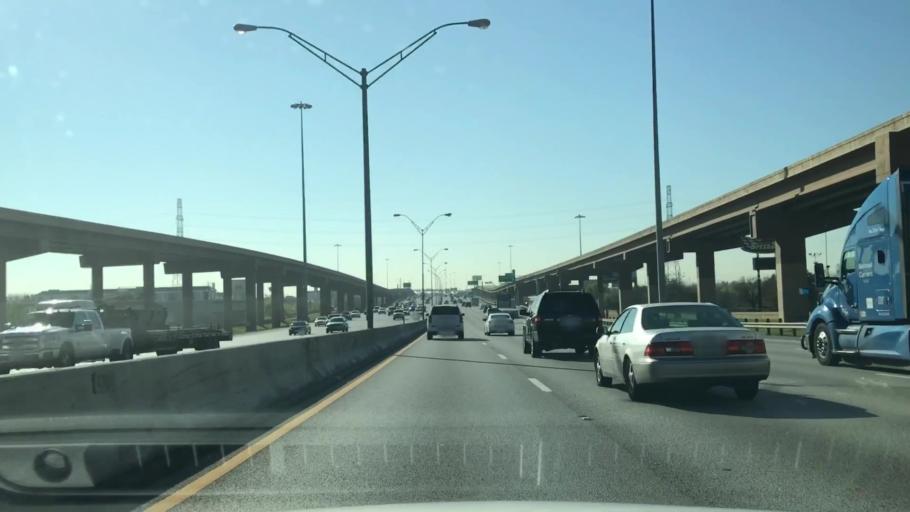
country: US
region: Texas
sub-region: Dallas County
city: Farmers Branch
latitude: 32.8860
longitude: -96.8982
